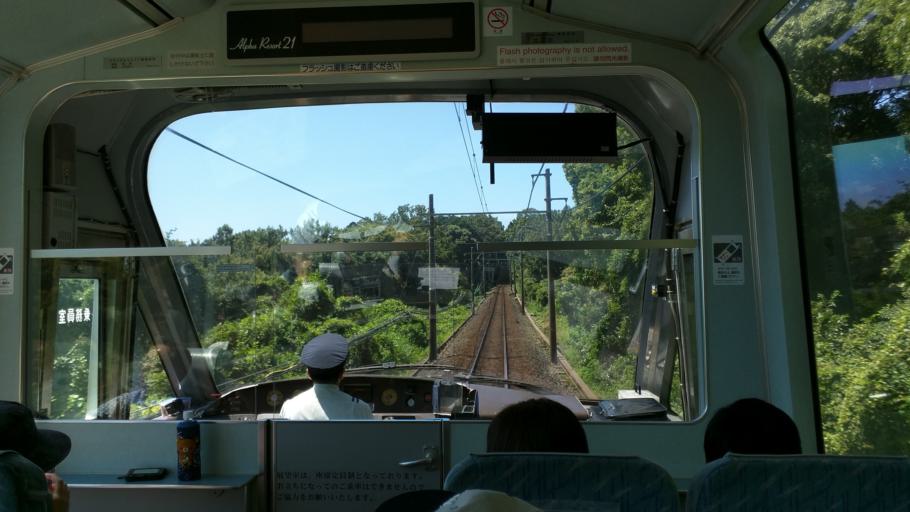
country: JP
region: Shizuoka
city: Ito
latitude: 34.9053
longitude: 139.1283
